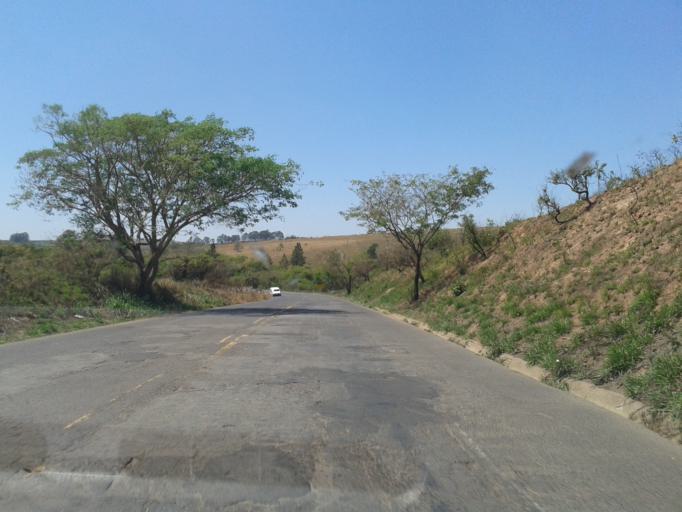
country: BR
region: Minas Gerais
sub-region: Araxa
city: Araxa
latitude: -19.4521
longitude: -47.1855
